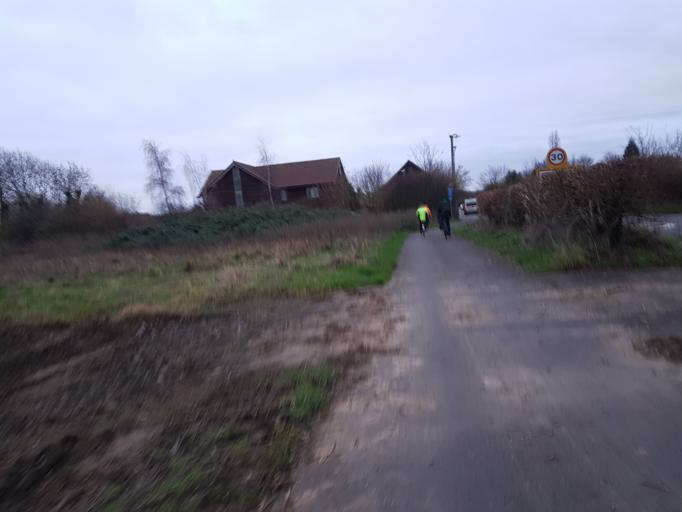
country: GB
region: England
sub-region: Cambridgeshire
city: Bottisham
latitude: 52.2245
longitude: 0.2271
